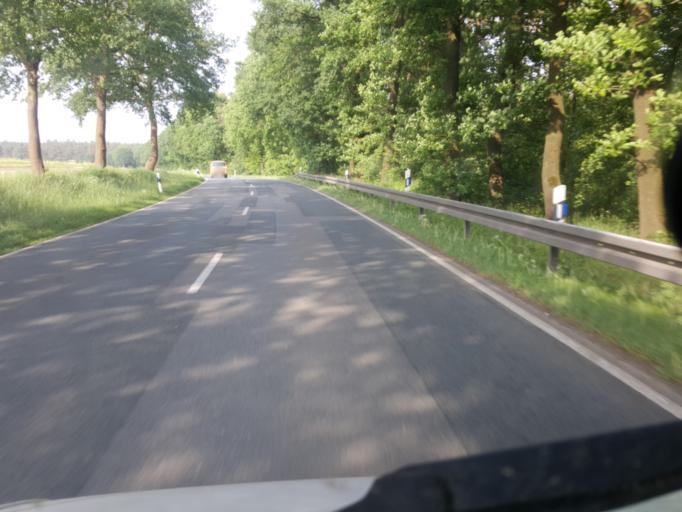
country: DE
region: Lower Saxony
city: Liebenau
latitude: 52.6133
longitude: 9.1083
